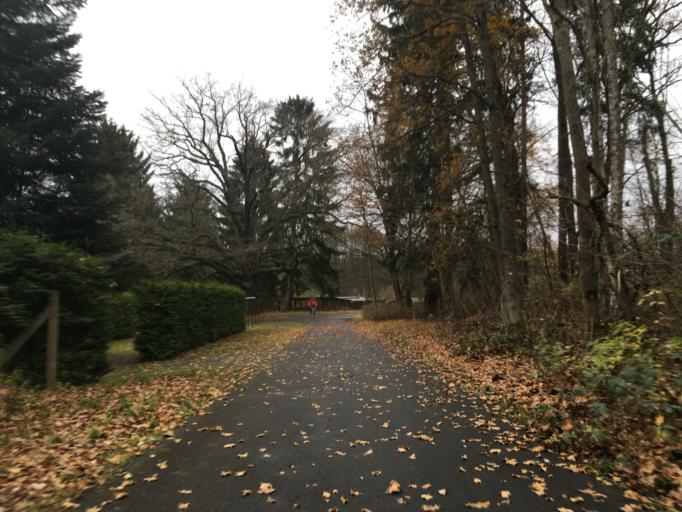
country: DE
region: Brandenburg
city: Mullrose
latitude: 52.2425
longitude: 14.4501
